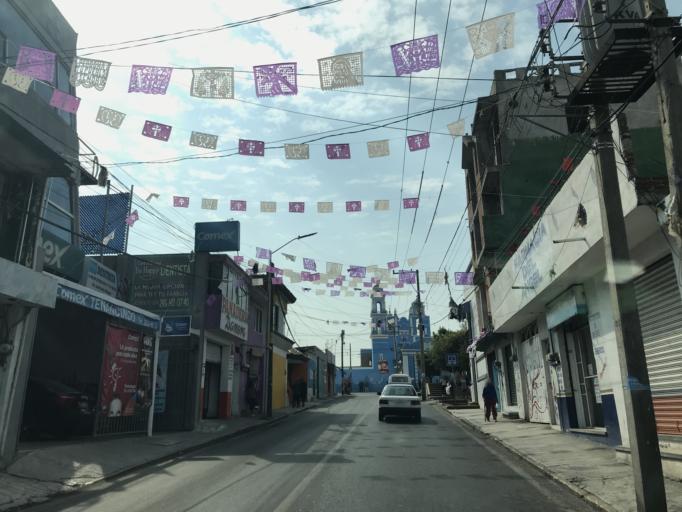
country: MX
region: Tlaxcala
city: Tenancingo
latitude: 19.1483
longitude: -98.2022
